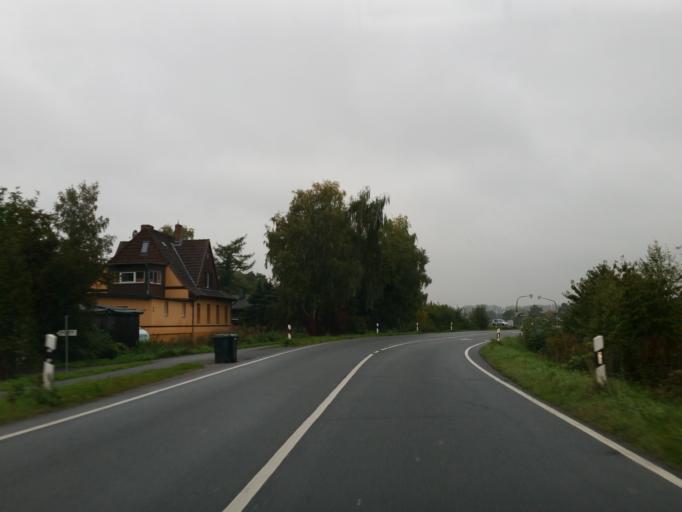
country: DE
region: Lower Saxony
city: Cremlingen
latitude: 52.2493
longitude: 10.5975
